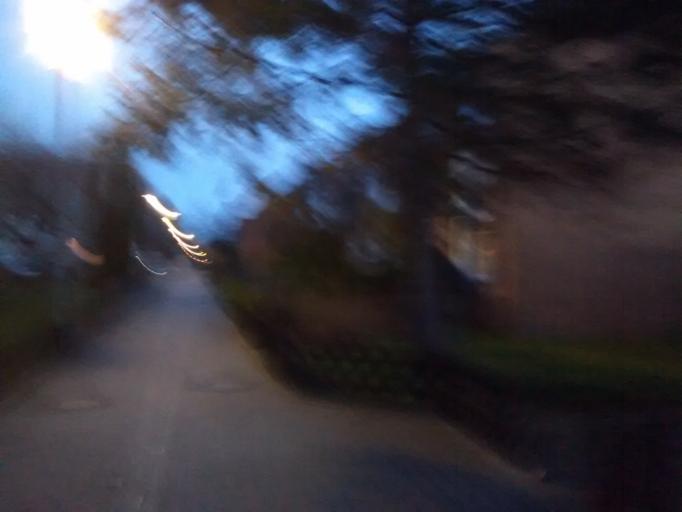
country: DE
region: Lower Saxony
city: Wolfenbuettel
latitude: 52.1690
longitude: 10.5215
